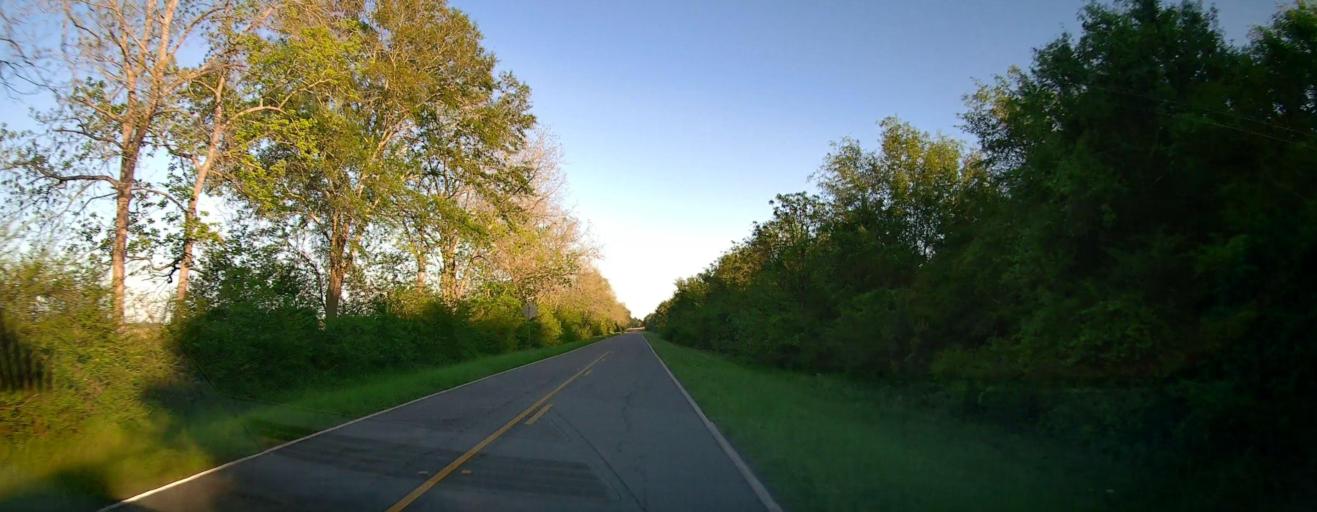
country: US
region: Georgia
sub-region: Ben Hill County
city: Fitzgerald
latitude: 31.6852
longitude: -83.2290
